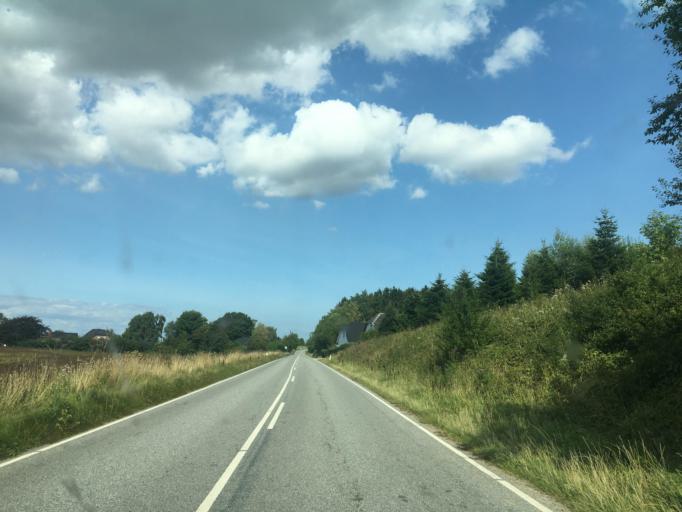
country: DK
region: South Denmark
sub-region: Middelfart Kommune
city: Ejby
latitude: 55.4081
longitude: 9.9138
